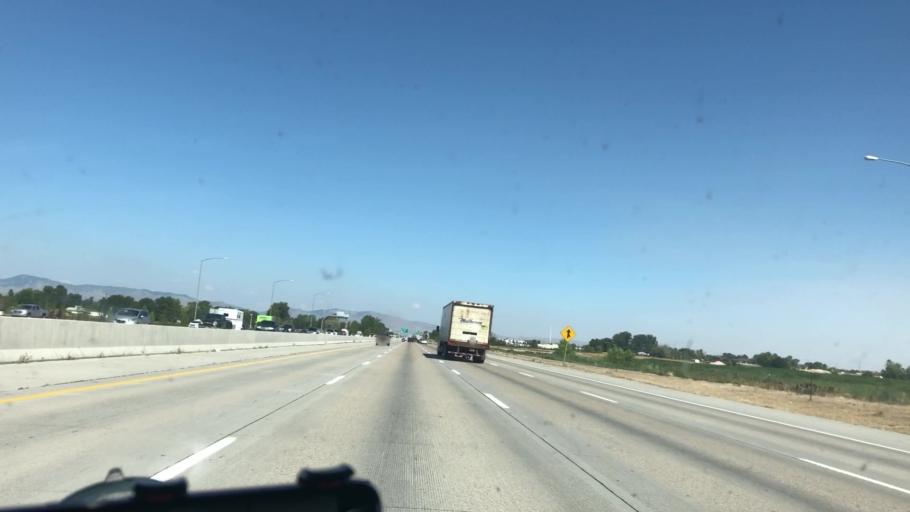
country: US
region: Idaho
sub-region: Ada County
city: Meridian
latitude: 43.5934
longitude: -116.4297
